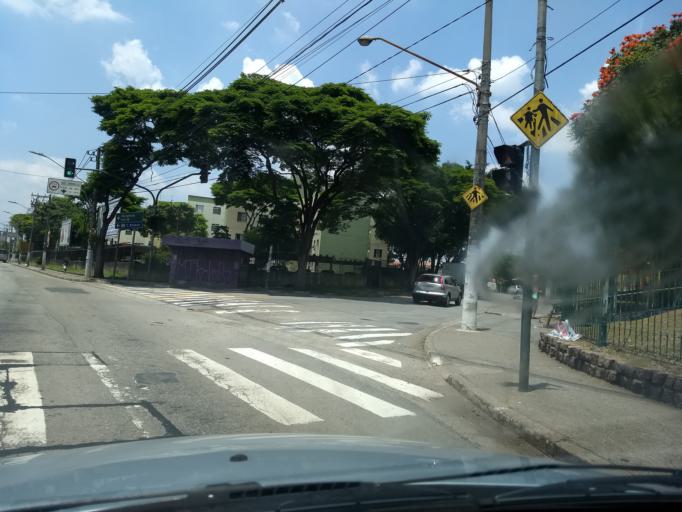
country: BR
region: Sao Paulo
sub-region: Osasco
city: Osasco
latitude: -23.5143
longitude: -46.7885
